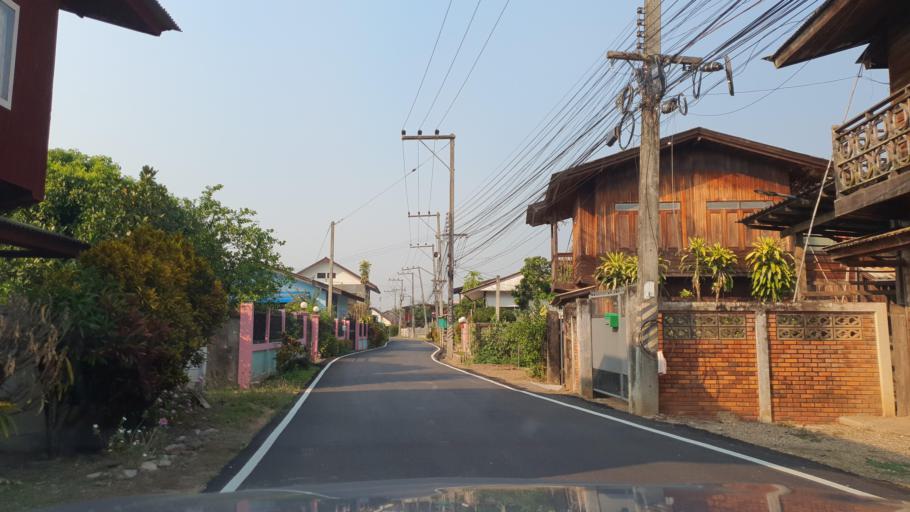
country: TH
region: Chiang Mai
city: Mae Taeng
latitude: 19.1394
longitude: 99.0104
